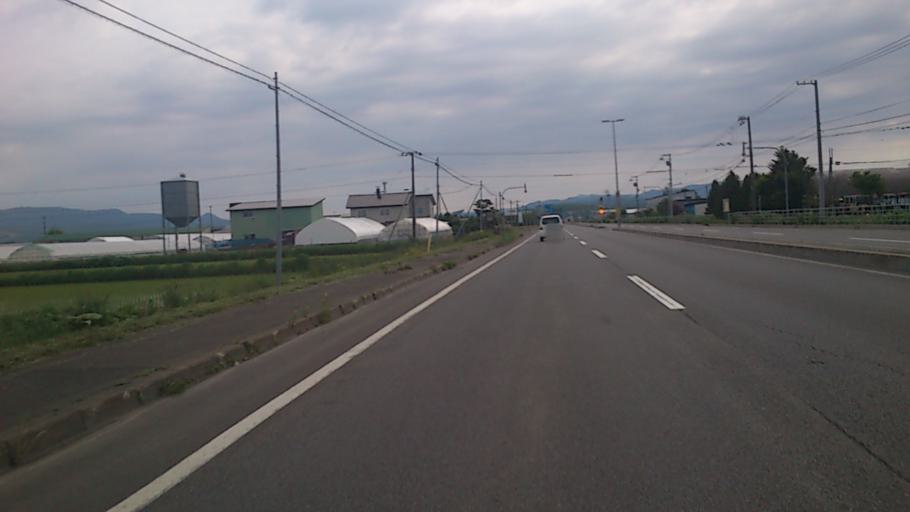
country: JP
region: Hokkaido
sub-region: Asahikawa-shi
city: Asahikawa
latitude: 43.8512
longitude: 142.4990
